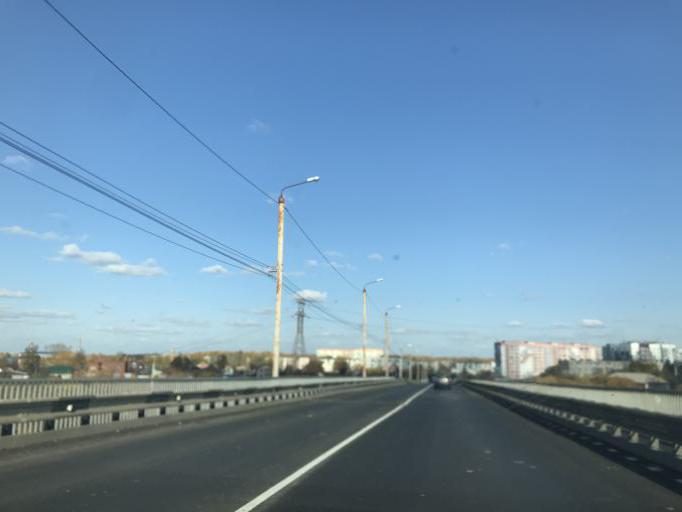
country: RU
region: Chelyabinsk
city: Roshchino
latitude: 55.2334
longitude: 61.2928
